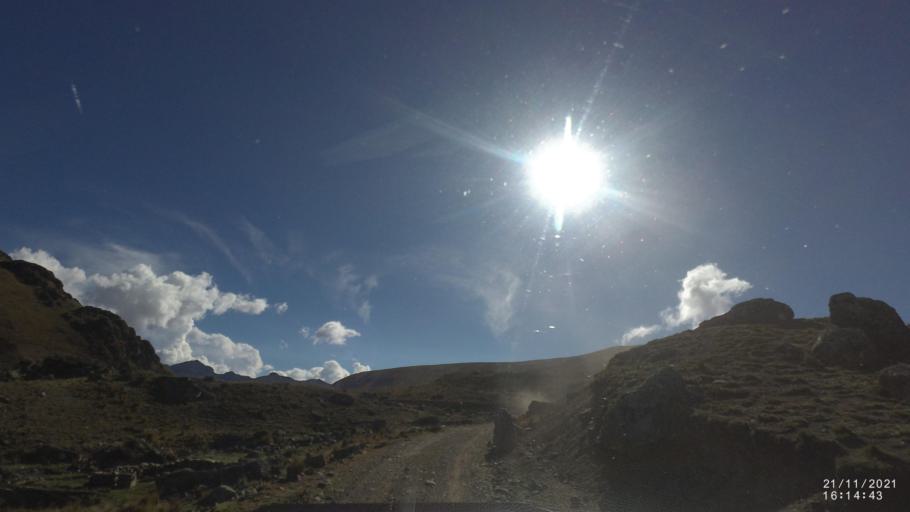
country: BO
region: Cochabamba
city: Cochabamba
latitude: -16.9980
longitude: -66.2764
